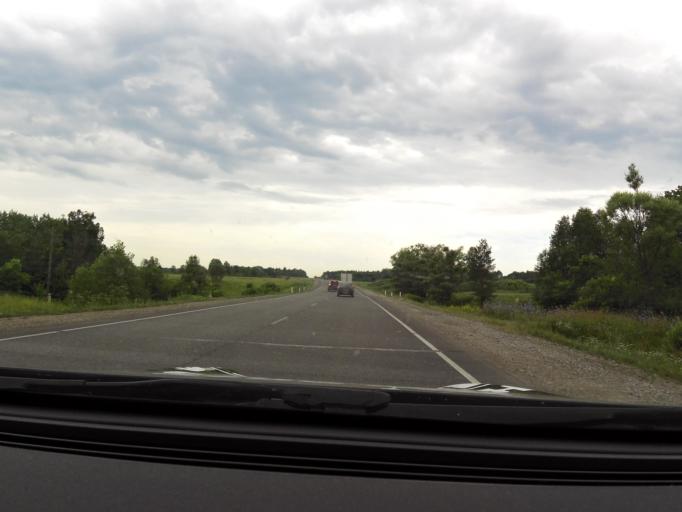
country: RU
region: Bashkortostan
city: Kudeyevskiy
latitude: 54.8164
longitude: 56.7052
